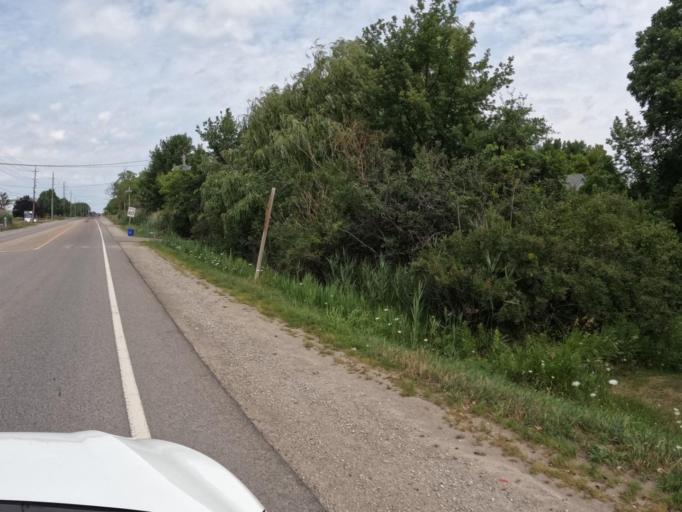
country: CA
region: Ontario
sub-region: Halton
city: Milton
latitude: 43.6388
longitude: -79.9356
